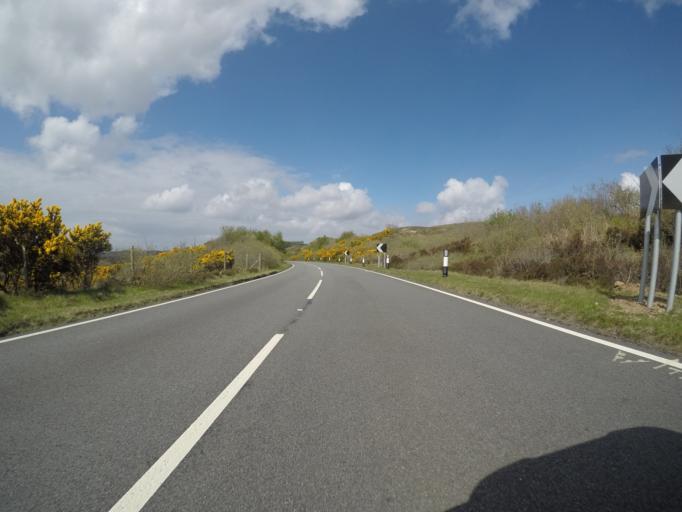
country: GB
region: Scotland
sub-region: Highland
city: Portree
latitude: 57.5202
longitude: -6.3409
